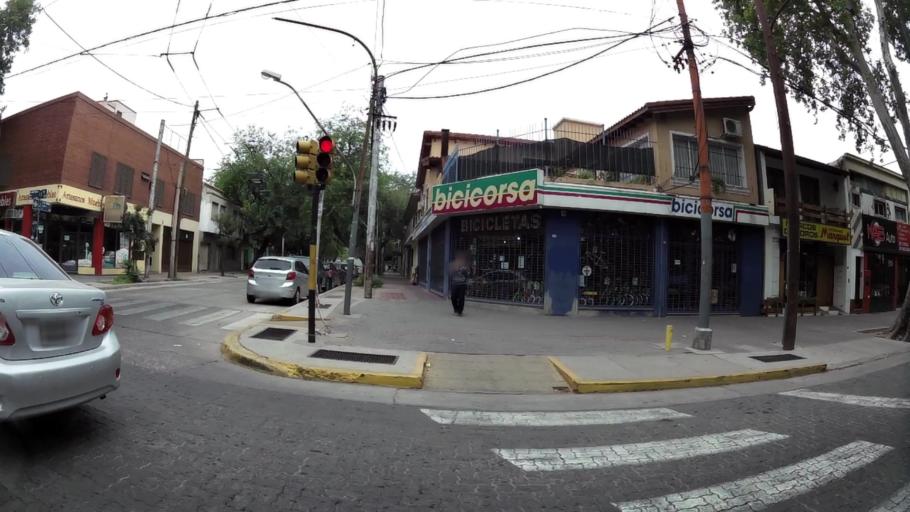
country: AR
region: Mendoza
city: Mendoza
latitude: -32.8778
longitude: -68.8361
